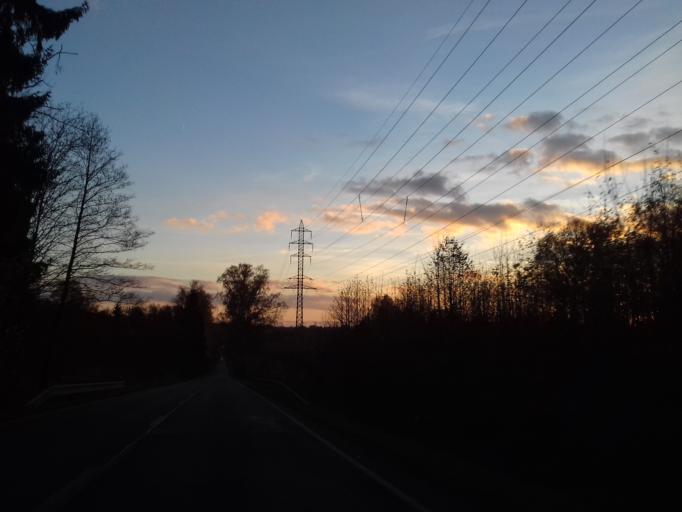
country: CZ
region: Pardubicky
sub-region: Okres Chrudim
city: Hlinsko
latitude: 49.7342
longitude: 15.8748
